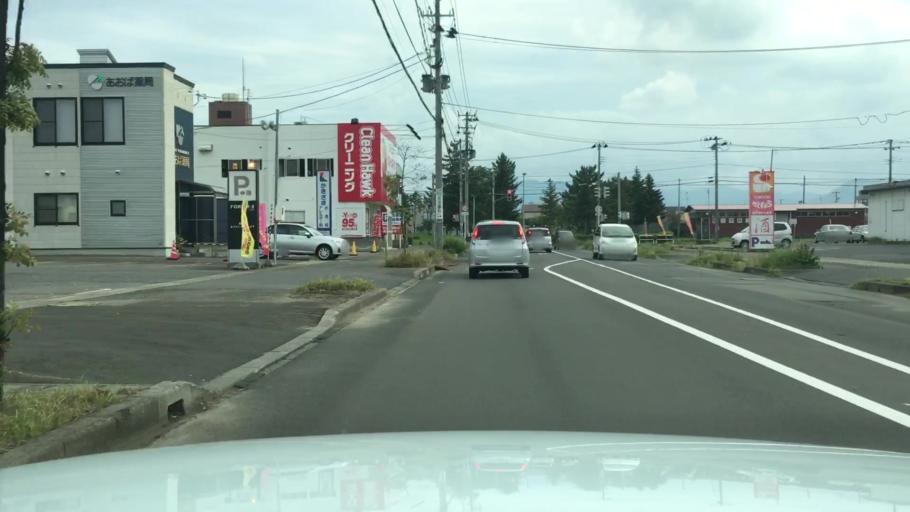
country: JP
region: Aomori
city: Hirosaki
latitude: 40.6183
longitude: 140.4844
